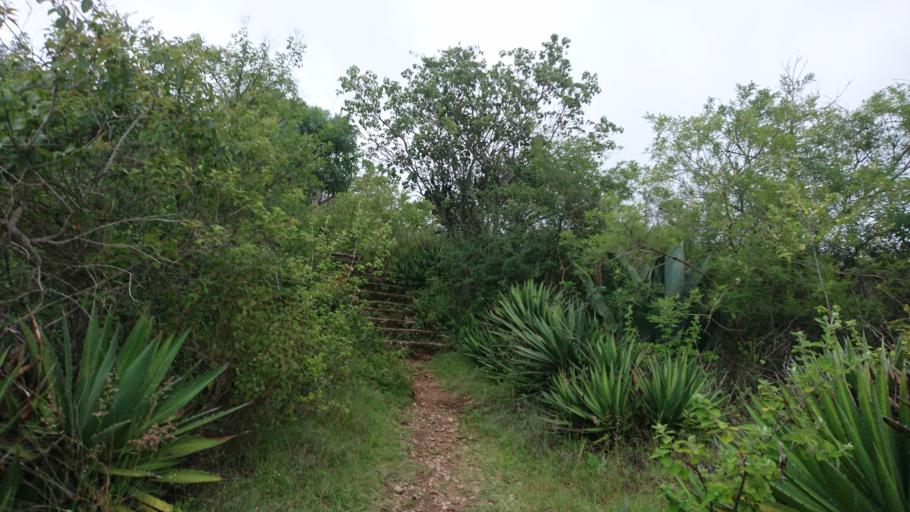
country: MX
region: Oaxaca
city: San Lorenzo Albarradas
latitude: 16.8688
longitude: -96.2738
